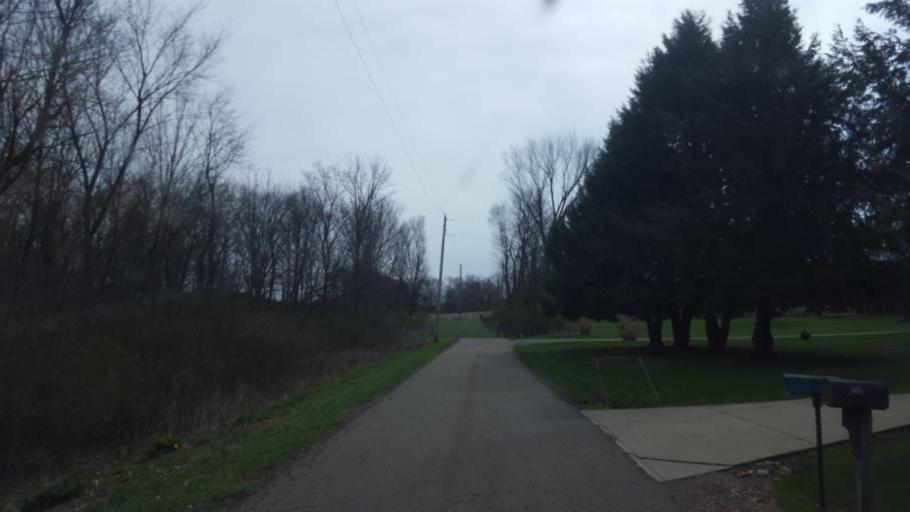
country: US
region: Ohio
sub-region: Knox County
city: Mount Vernon
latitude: 40.3806
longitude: -82.4609
